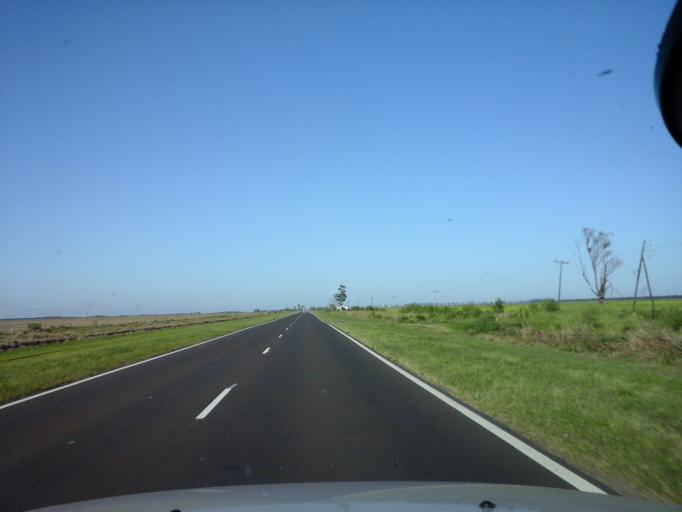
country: AR
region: Corrientes
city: Ita Ibate
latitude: -27.4510
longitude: -57.4106
